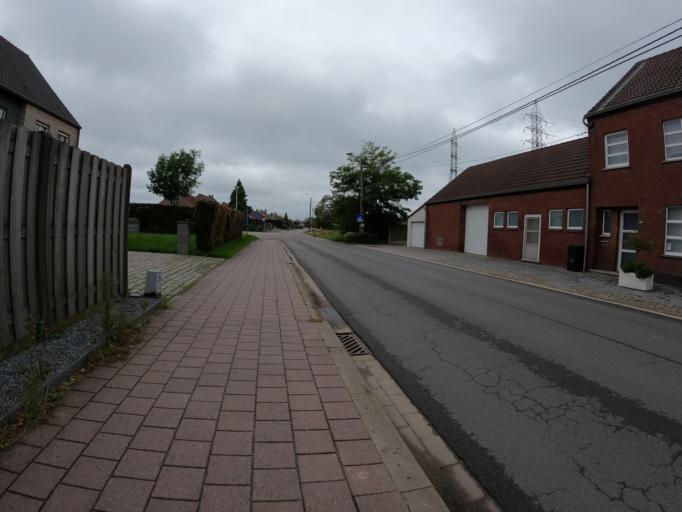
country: BE
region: Flanders
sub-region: Provincie Antwerpen
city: Heist-op-den-Berg
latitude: 51.0549
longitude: 4.7059
